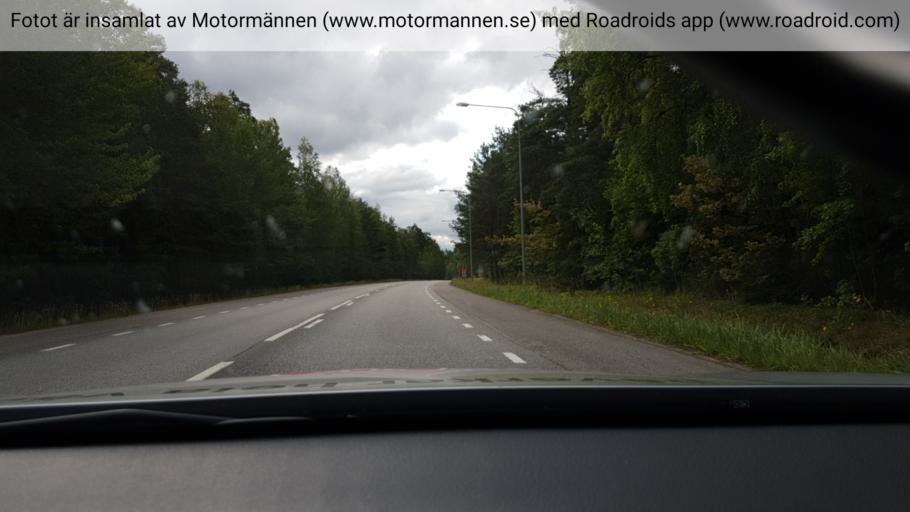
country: SE
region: Stockholm
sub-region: Nacka Kommun
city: Alta
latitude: 59.2379
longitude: 18.1881
